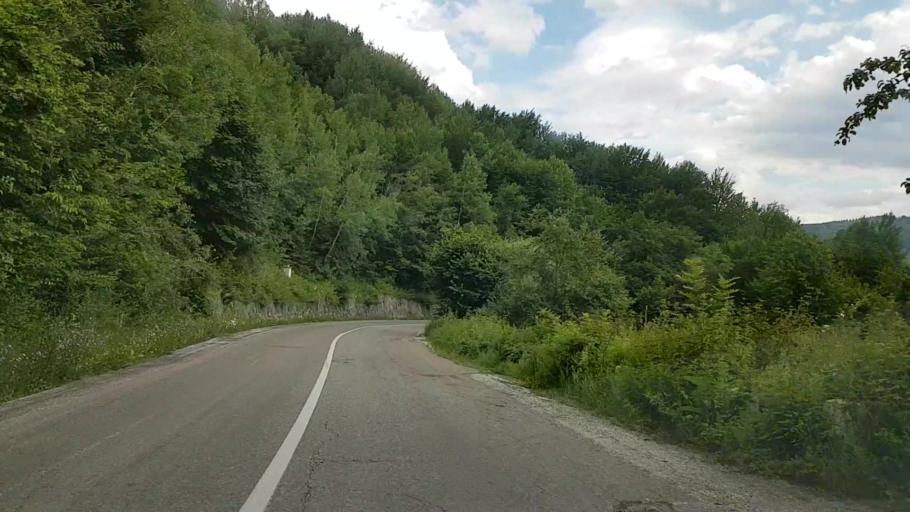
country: RO
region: Neamt
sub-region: Comuna Pangarati
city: Pangarati
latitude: 46.9604
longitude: 26.1223
